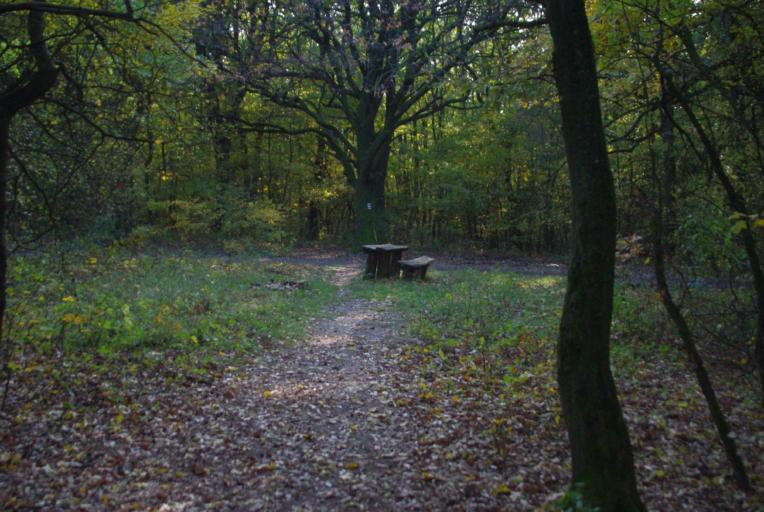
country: HU
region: Pest
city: Nagymaros
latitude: 47.8286
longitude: 18.9445
